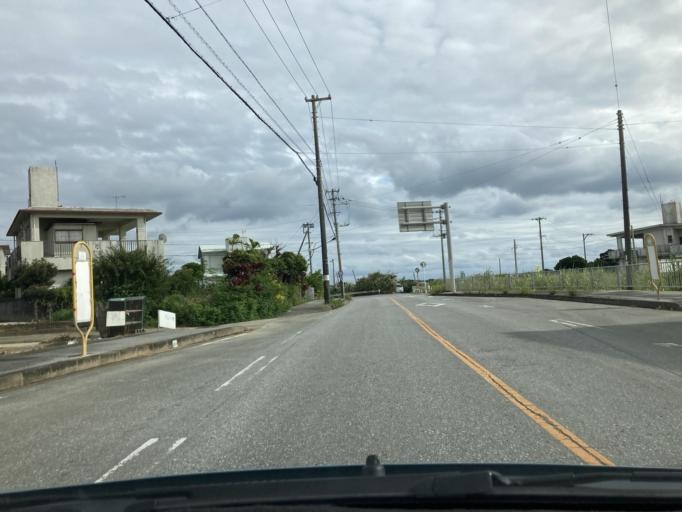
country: JP
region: Okinawa
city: Itoman
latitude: 26.1170
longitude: 127.6955
